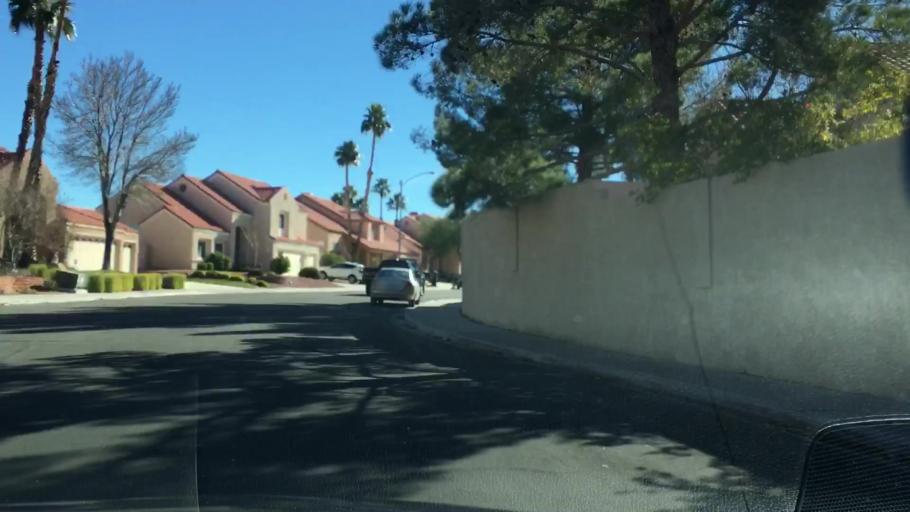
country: US
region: Nevada
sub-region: Clark County
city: Whitney
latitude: 36.0600
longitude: -115.0629
